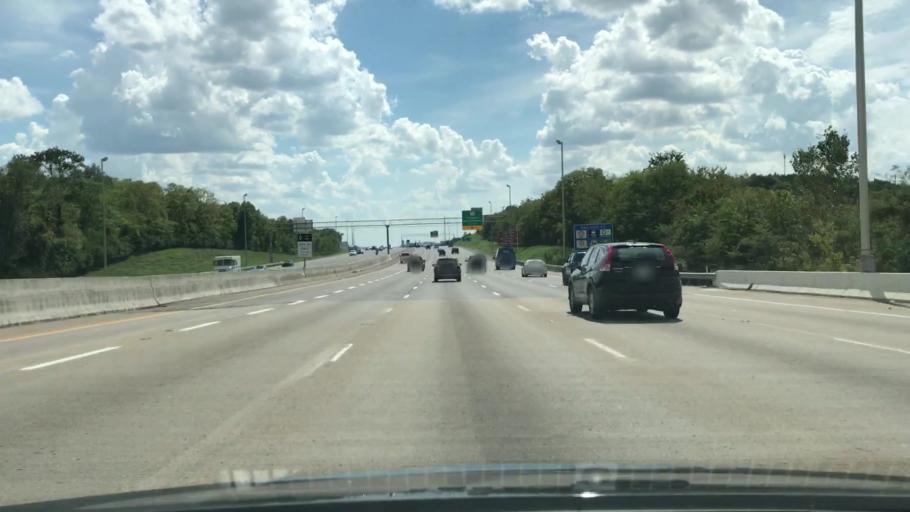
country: US
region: Tennessee
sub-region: Williamson County
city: Franklin
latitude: 35.9262
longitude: -86.8218
